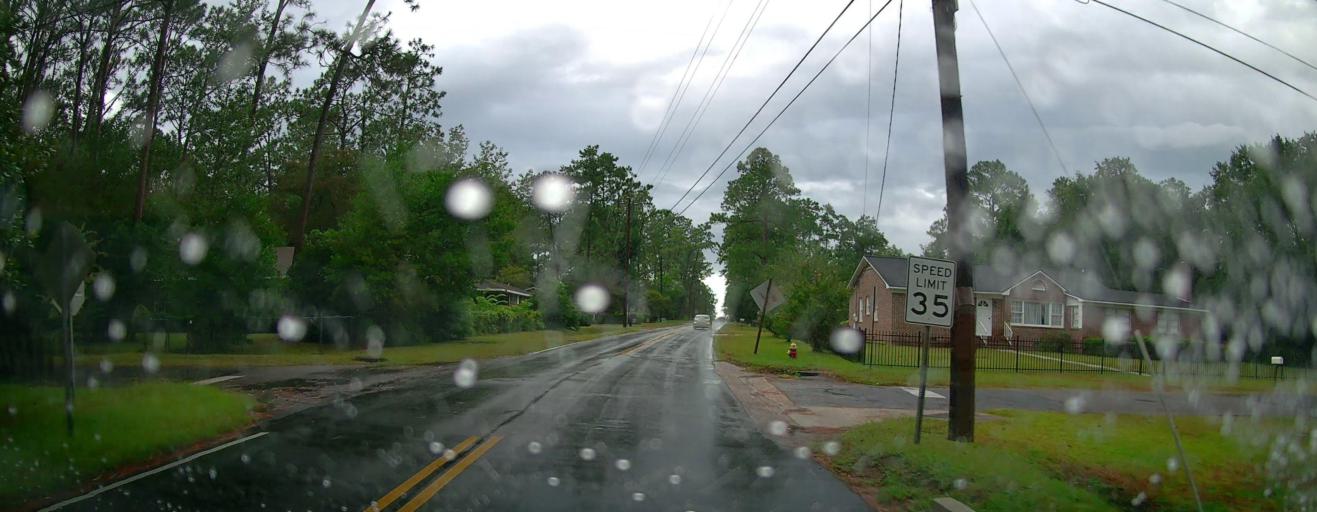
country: US
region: Georgia
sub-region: Ware County
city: Sunnyside
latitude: 31.2251
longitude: -82.3274
